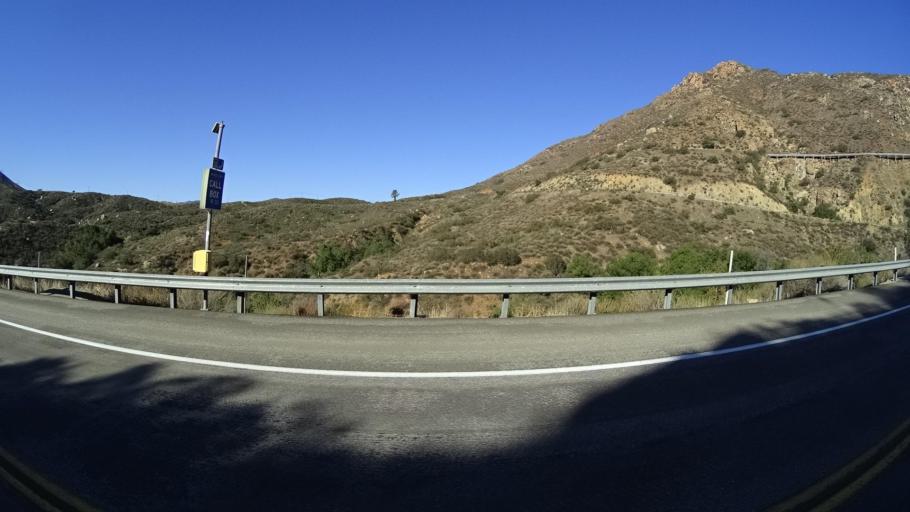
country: MX
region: Baja California
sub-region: Tecate
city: Lomas de Santa Anita
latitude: 32.6171
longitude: -116.7273
